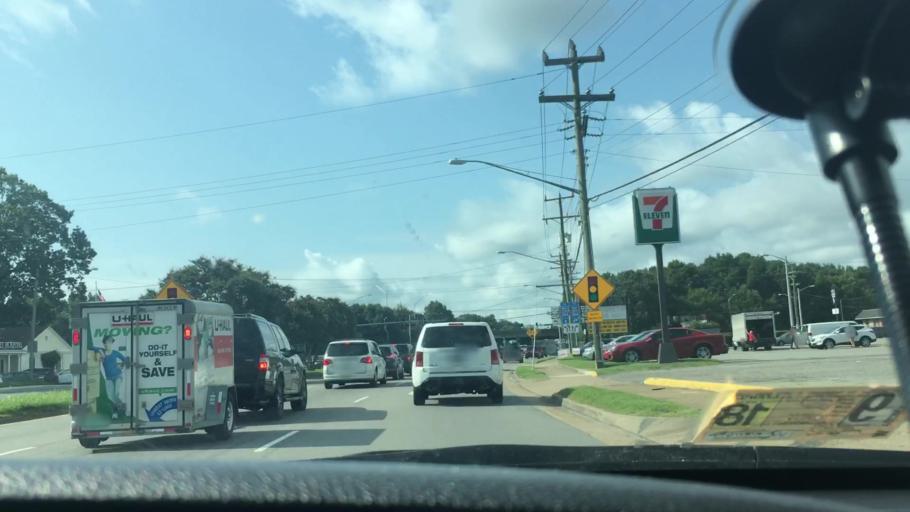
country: US
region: Virginia
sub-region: City of Virginia Beach
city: Virginia Beach
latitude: 36.8432
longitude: -76.0480
